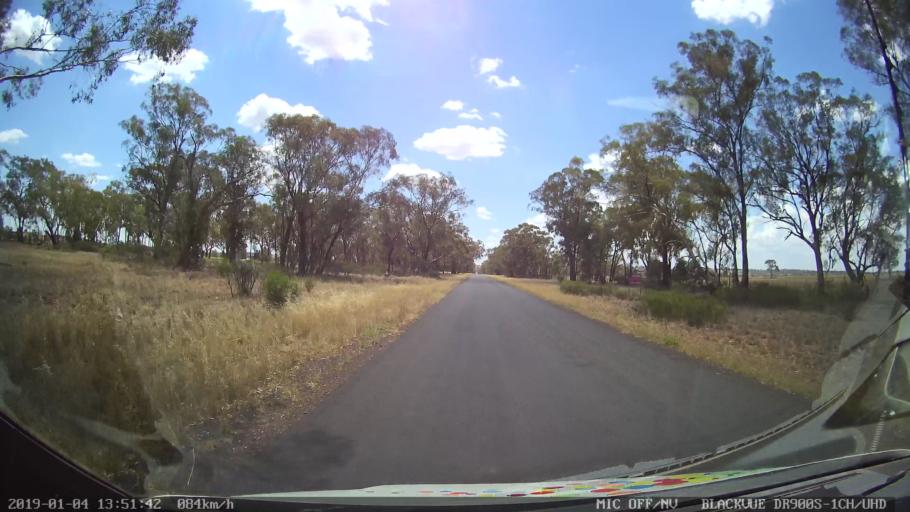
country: AU
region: New South Wales
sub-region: Dubbo Municipality
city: Dubbo
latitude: -32.4036
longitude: 148.5711
